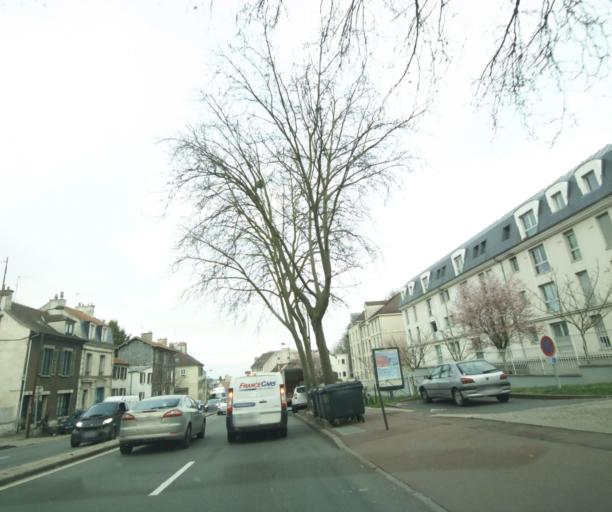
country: FR
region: Ile-de-France
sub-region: Departement des Yvelines
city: Le Port-Marly
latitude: 48.8777
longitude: 2.1071
